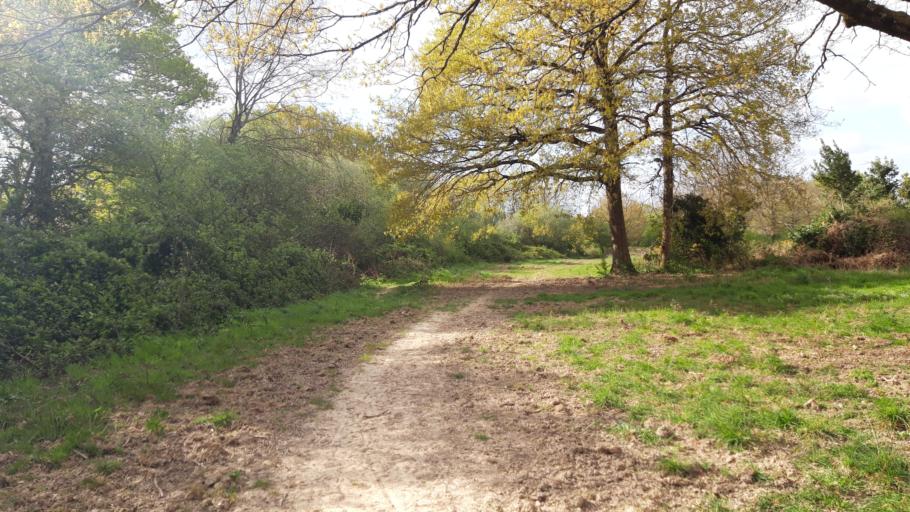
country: FR
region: Pays de la Loire
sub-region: Departement de la Loire-Atlantique
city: Orvault
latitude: 47.2321
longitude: -1.6068
